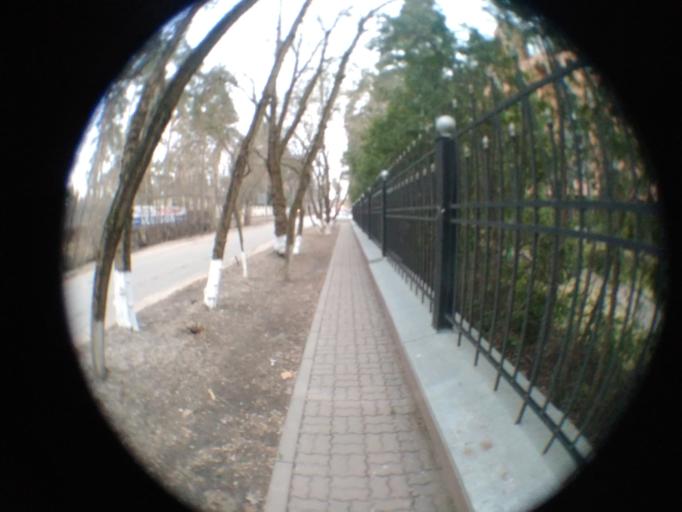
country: RU
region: Moskovskaya
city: Zhukovskiy
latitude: 55.5835
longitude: 38.1482
